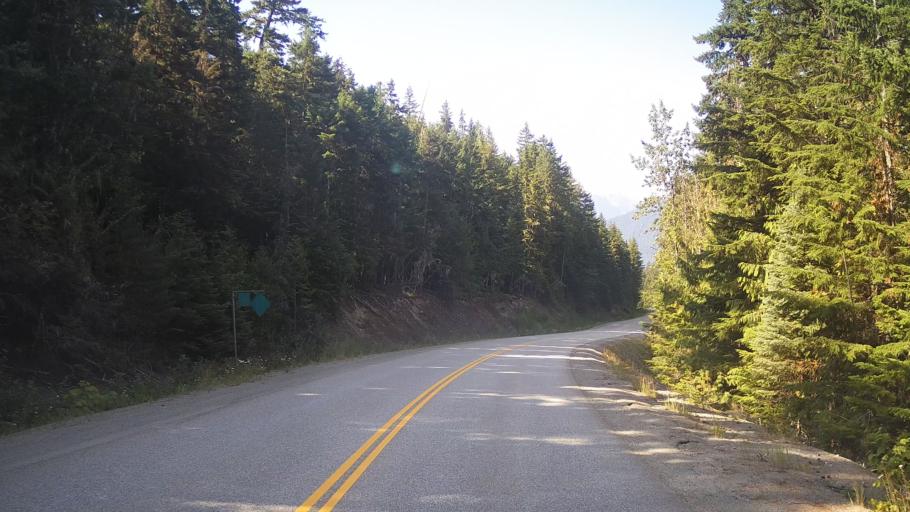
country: CA
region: British Columbia
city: Pemberton
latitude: 50.3306
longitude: -122.5521
